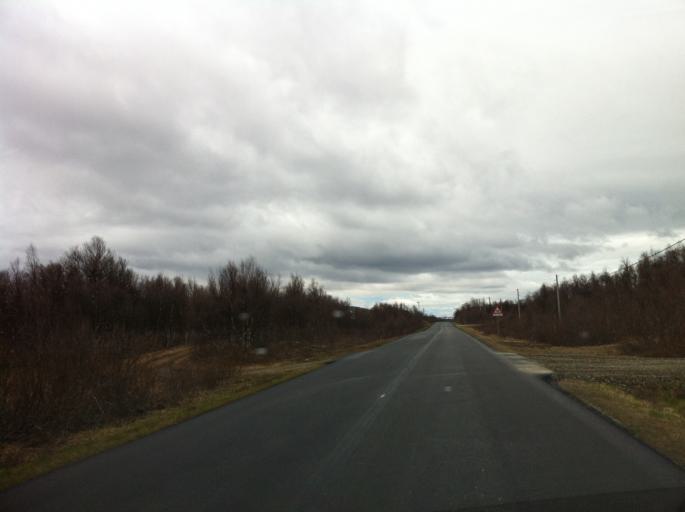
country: NO
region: Sor-Trondelag
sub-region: Tydal
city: Aas
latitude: 62.6402
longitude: 12.0108
